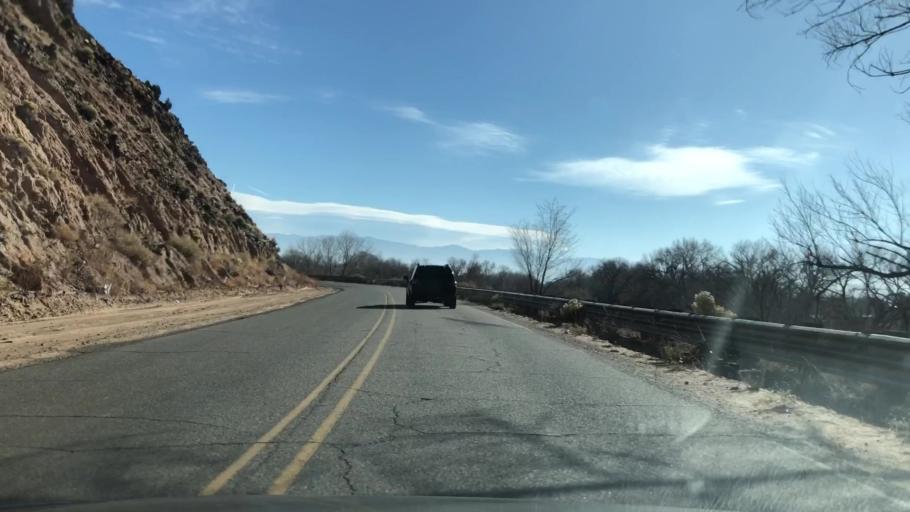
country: US
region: New Mexico
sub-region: Rio Arriba County
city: Ohkay Owingeh
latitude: 36.0847
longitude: -106.1262
